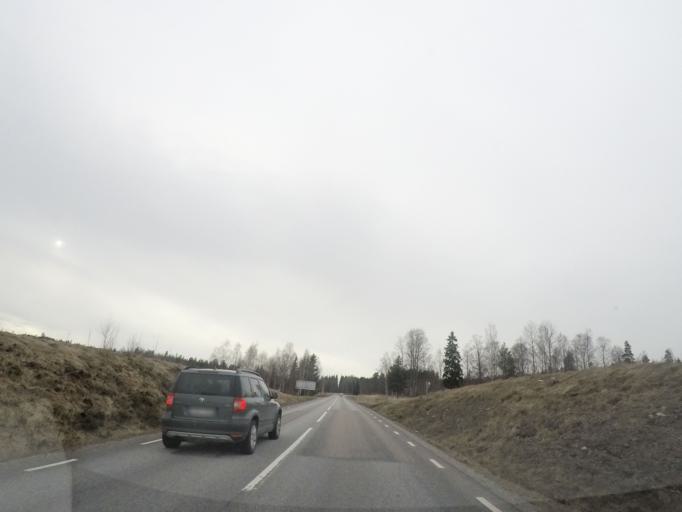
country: SE
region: Vaestmanland
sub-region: Skinnskattebergs Kommun
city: Skinnskatteberg
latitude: 59.8749
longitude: 15.6444
